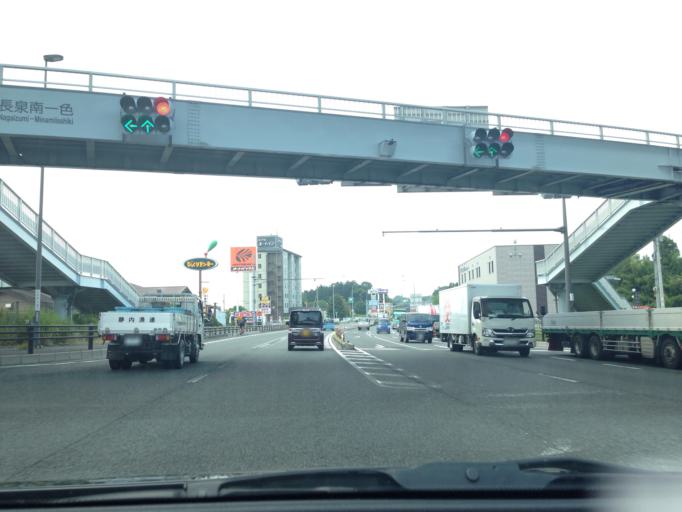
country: JP
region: Shizuoka
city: Mishima
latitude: 35.1511
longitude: 138.8937
